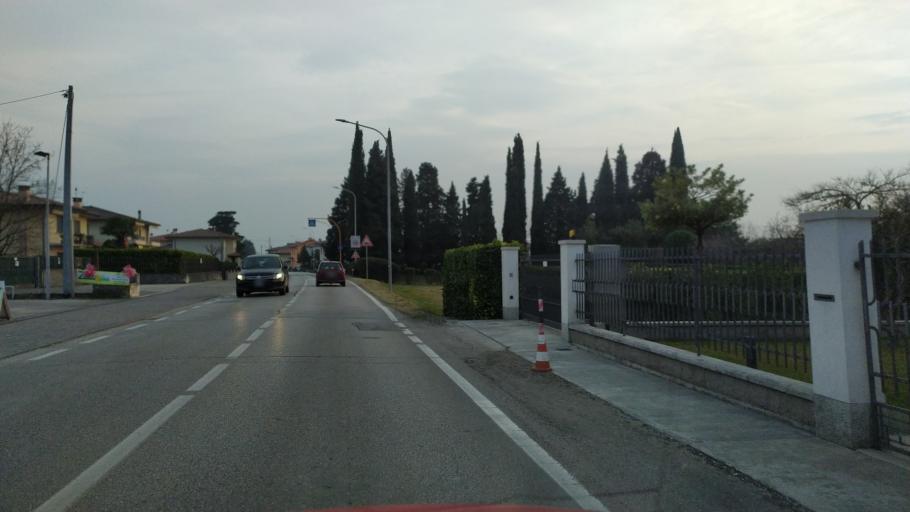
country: IT
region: Veneto
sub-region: Provincia di Vicenza
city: Sarcedo
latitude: 45.6990
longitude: 11.5313
